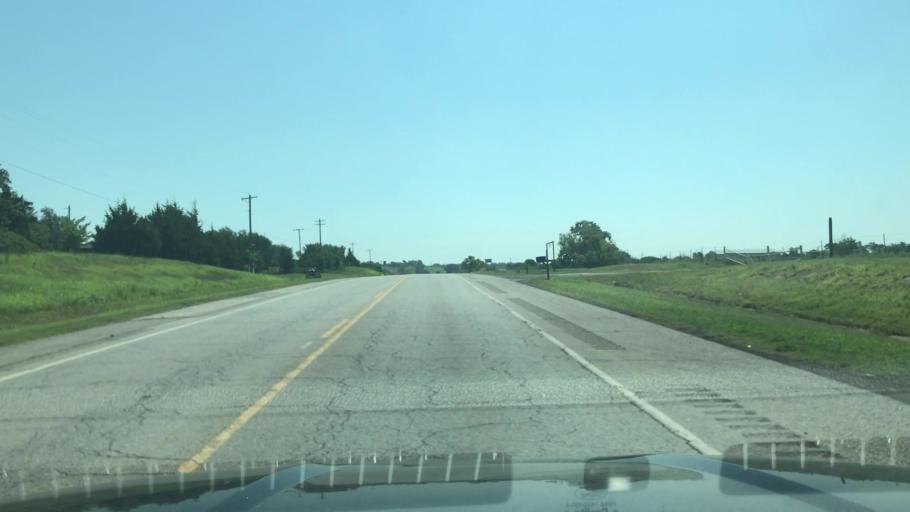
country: US
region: Oklahoma
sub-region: Creek County
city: Drumright
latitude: 35.9884
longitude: -96.5630
